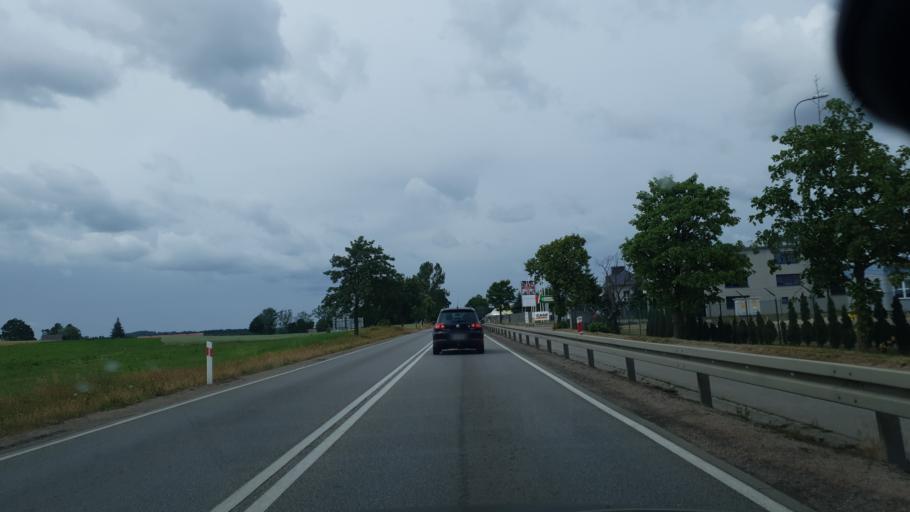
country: PL
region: Pomeranian Voivodeship
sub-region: Powiat kartuski
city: Zukowo
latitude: 54.3825
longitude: 18.3614
